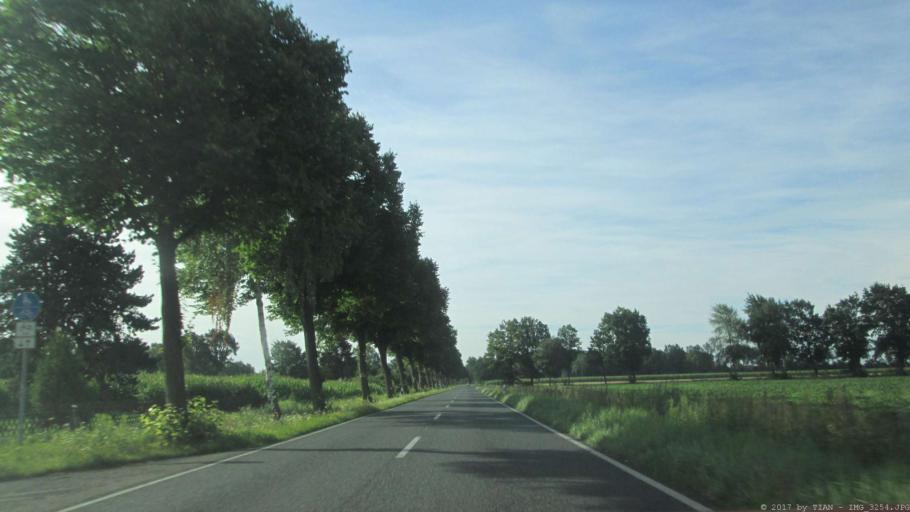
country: DE
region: Lower Saxony
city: Wolfsburg
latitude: 52.4566
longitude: 10.8261
